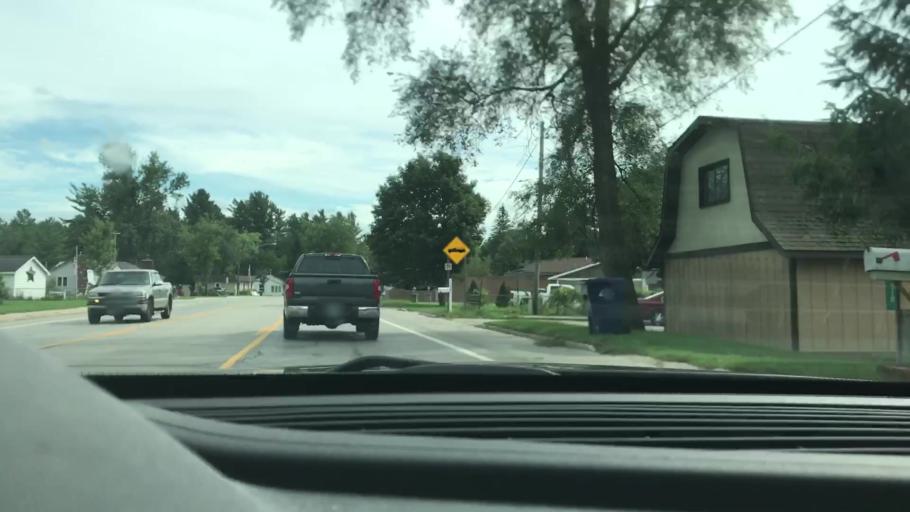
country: US
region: Michigan
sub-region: Missaukee County
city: Lake City
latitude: 44.3256
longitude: -85.2124
